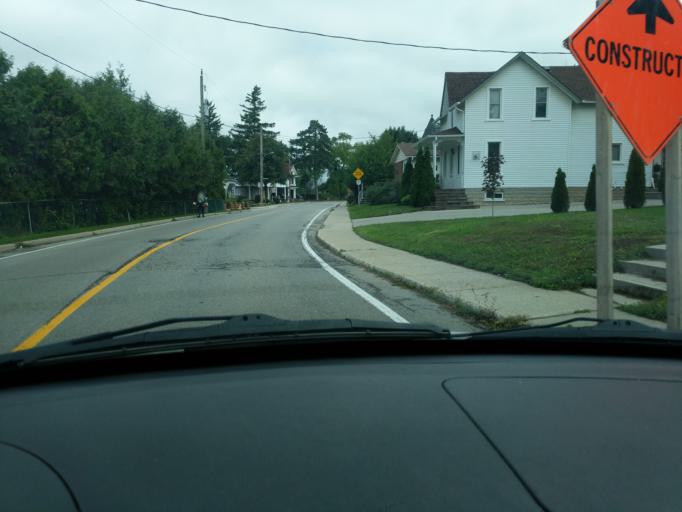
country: CA
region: Ontario
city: Cambridge
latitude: 43.4284
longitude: -80.3098
